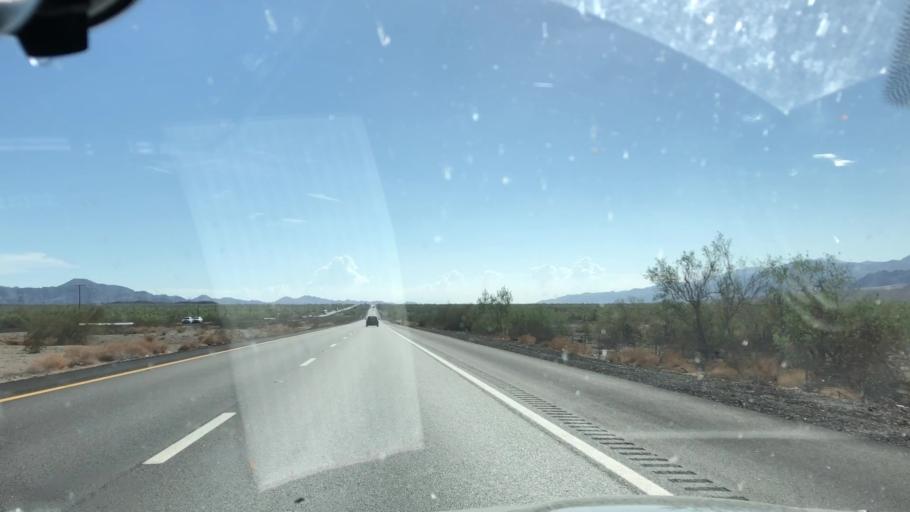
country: US
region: California
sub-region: Imperial County
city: Niland
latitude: 33.6942
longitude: -115.4908
